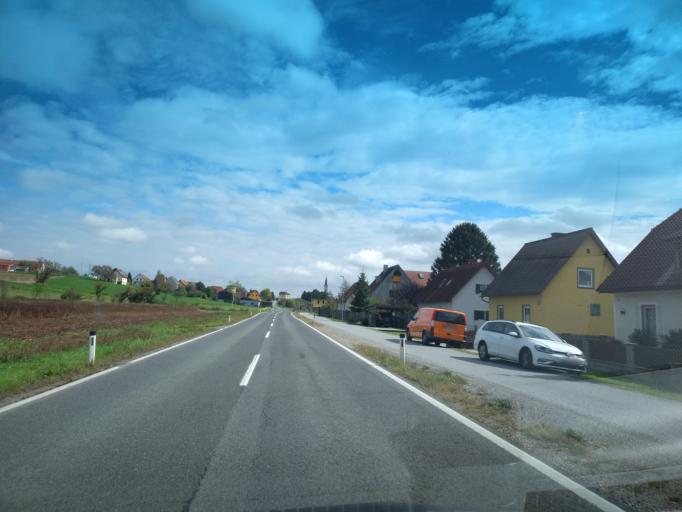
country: AT
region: Styria
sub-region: Politischer Bezirk Deutschlandsberg
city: Gross Sankt Florian
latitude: 46.8225
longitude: 15.3038
